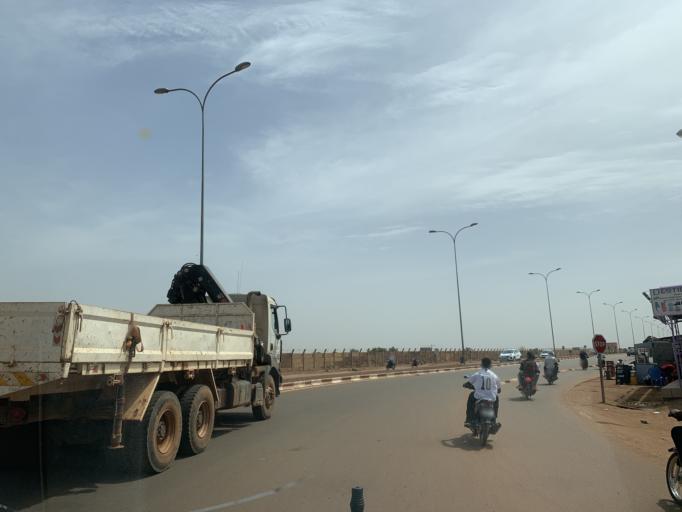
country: BF
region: Centre
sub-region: Kadiogo Province
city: Ouagadougou
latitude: 12.3359
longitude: -1.5199
